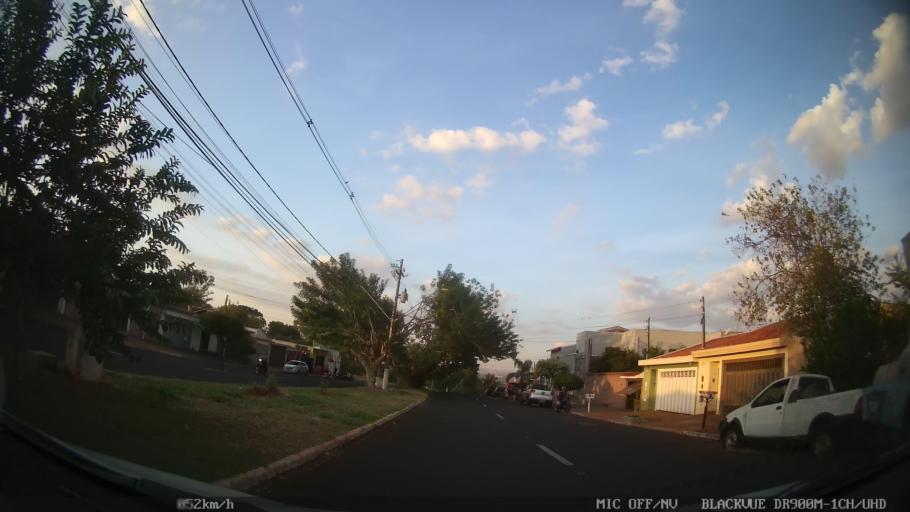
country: BR
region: Sao Paulo
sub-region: Ribeirao Preto
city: Ribeirao Preto
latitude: -21.1346
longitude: -47.8450
